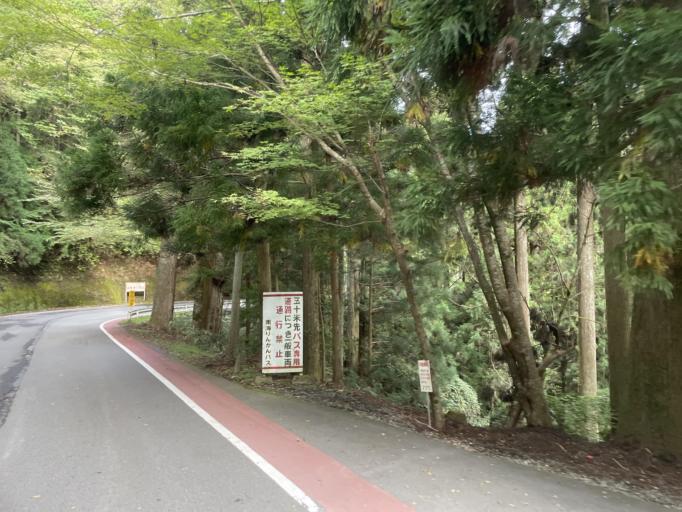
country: JP
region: Wakayama
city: Koya
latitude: 34.2200
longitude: 135.5805
